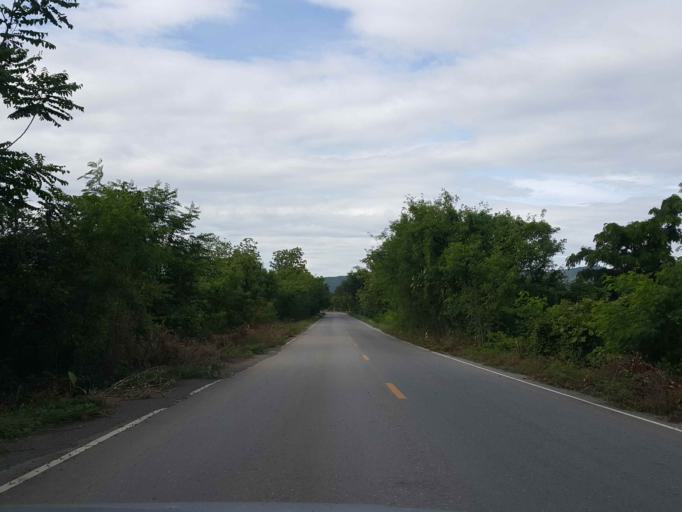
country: TH
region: Sukhothai
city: Thung Saliam
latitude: 17.2469
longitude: 99.5175
